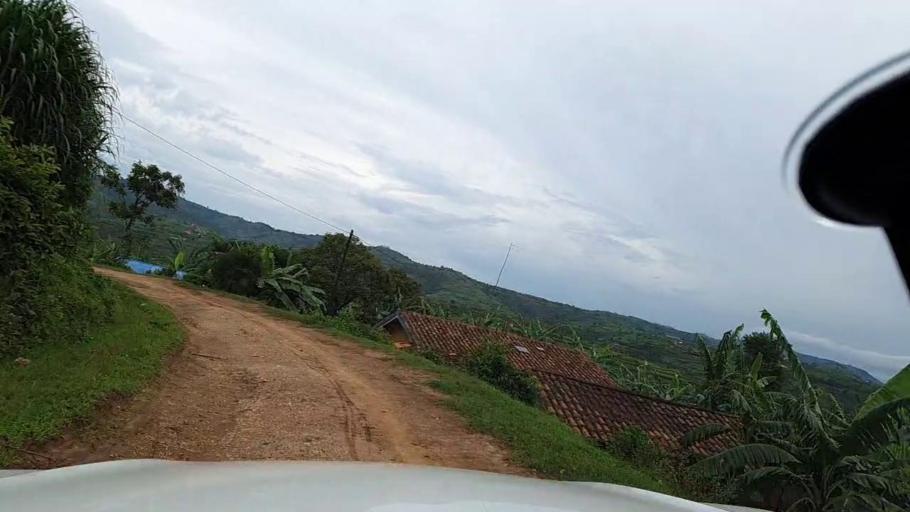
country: RW
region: Southern Province
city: Gitarama
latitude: -2.0917
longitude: 29.6369
